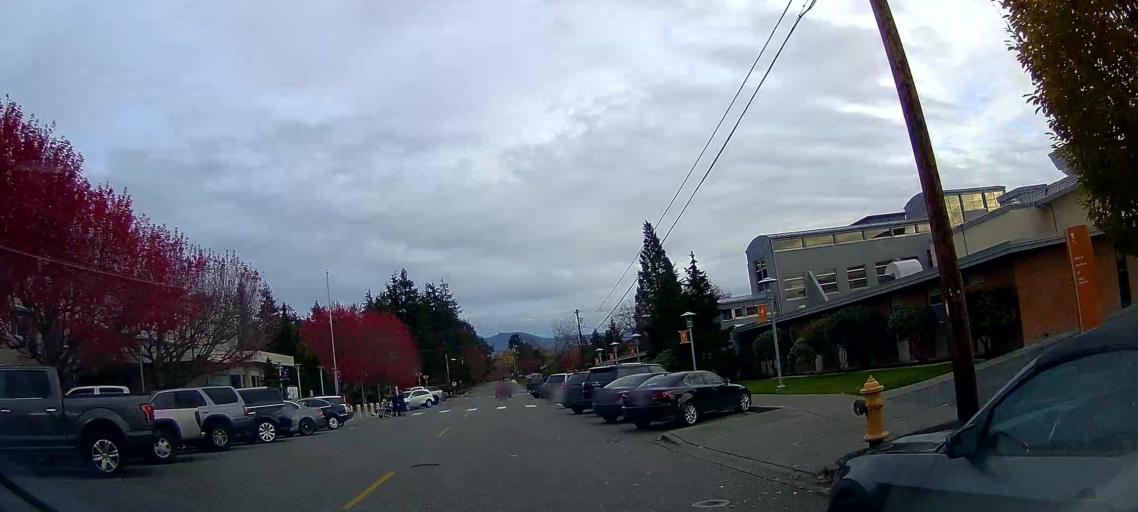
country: US
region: Washington
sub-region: Skagit County
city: Mount Vernon
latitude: 48.4175
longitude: -122.3244
